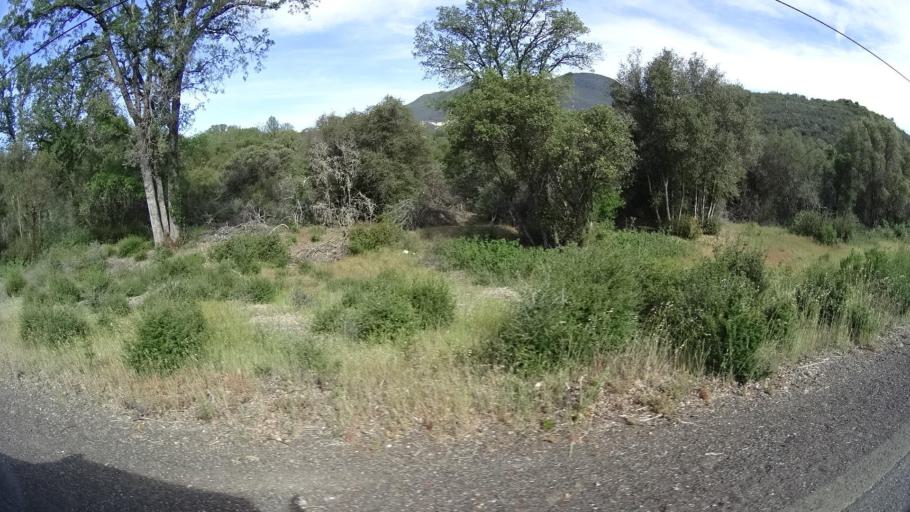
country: US
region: California
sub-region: Lake County
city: Soda Bay
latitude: 38.9441
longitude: -122.7361
